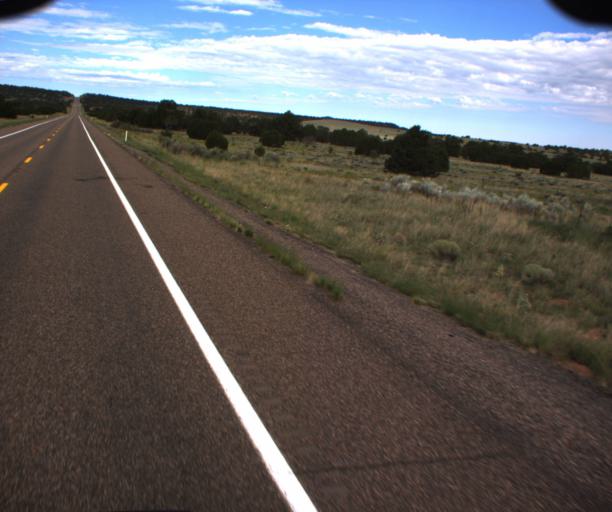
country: US
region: Arizona
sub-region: Apache County
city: Springerville
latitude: 34.1530
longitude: -109.1503
